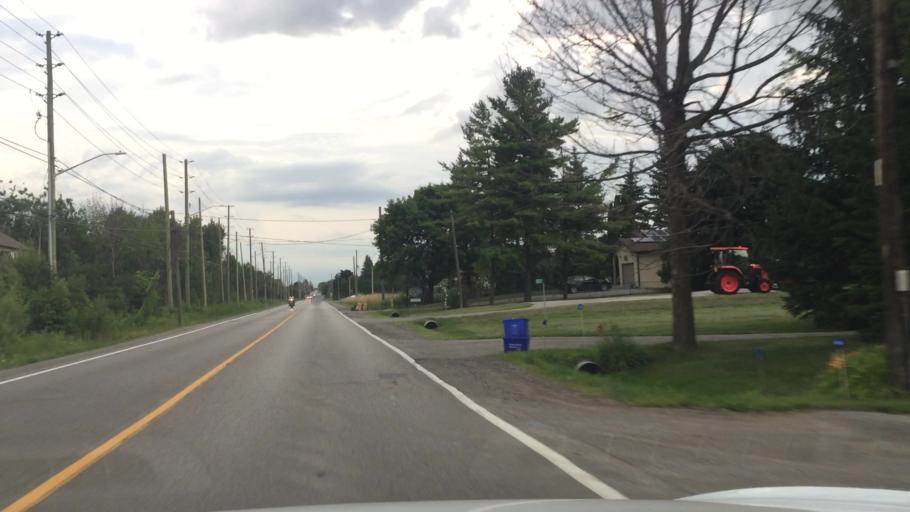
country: CA
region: Ontario
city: Oshawa
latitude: 43.9244
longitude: -78.8212
